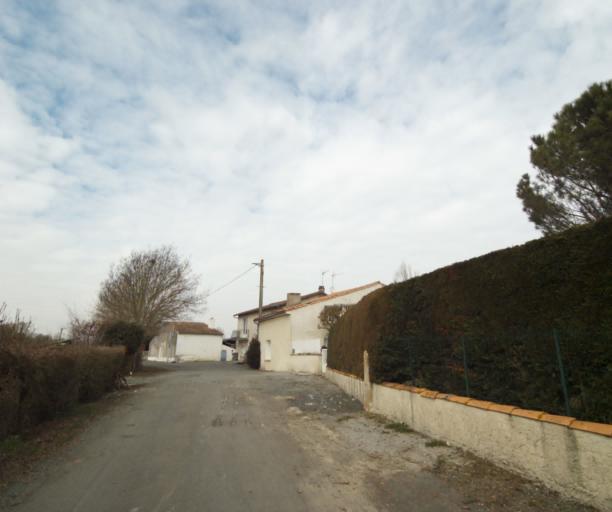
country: FR
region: Poitou-Charentes
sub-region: Departement des Deux-Sevres
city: Saint-Symphorien
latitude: 46.2879
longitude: -0.4768
